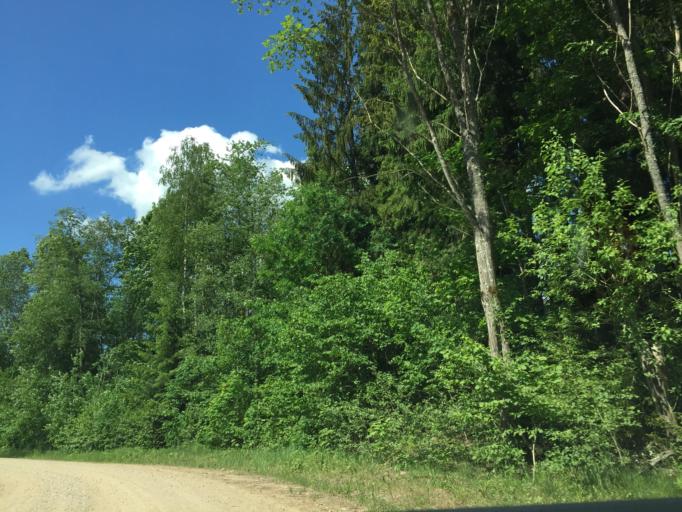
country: LV
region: Priekuli
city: Priekuli
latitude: 57.2423
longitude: 25.4125
